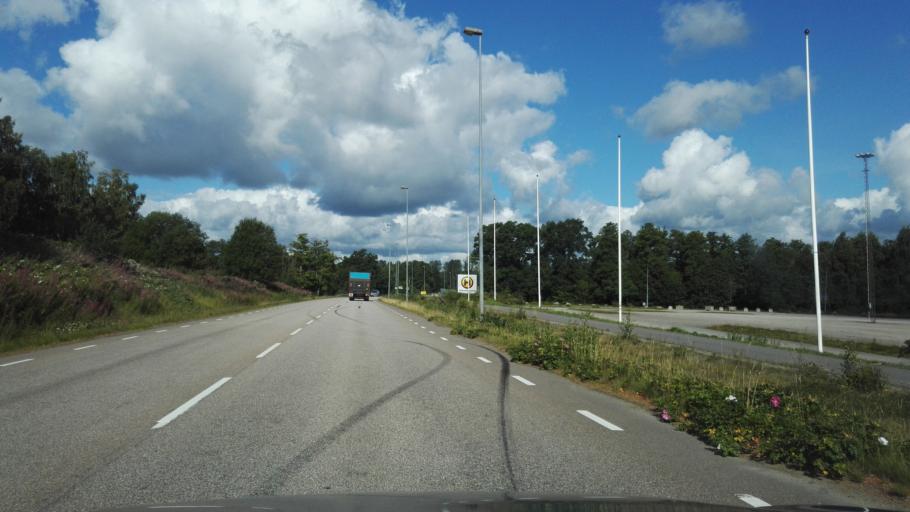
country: SE
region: Kronoberg
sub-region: Vaxjo Kommun
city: Vaexjoe
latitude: 56.8793
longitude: 14.7413
